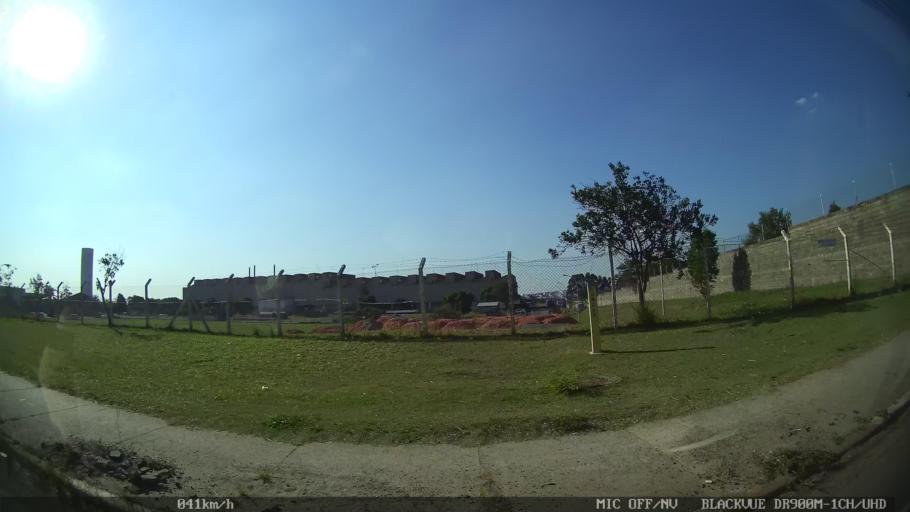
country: BR
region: Sao Paulo
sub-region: Campinas
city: Campinas
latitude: -22.9932
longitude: -47.1335
